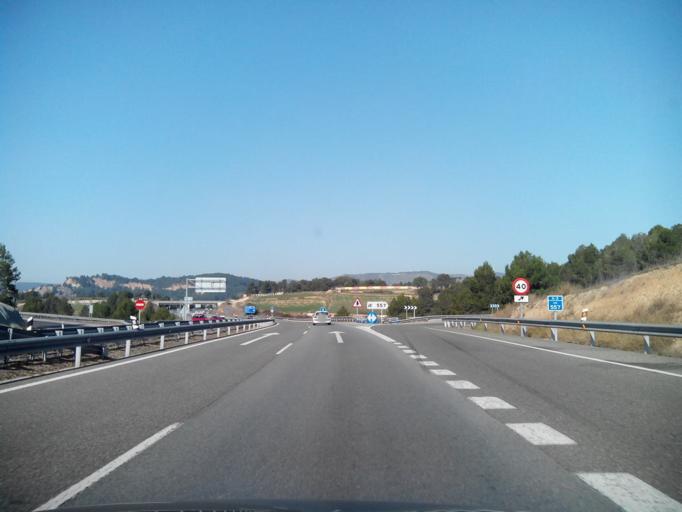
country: ES
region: Catalonia
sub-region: Provincia de Barcelona
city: Odena
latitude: 41.5932
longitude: 1.6498
